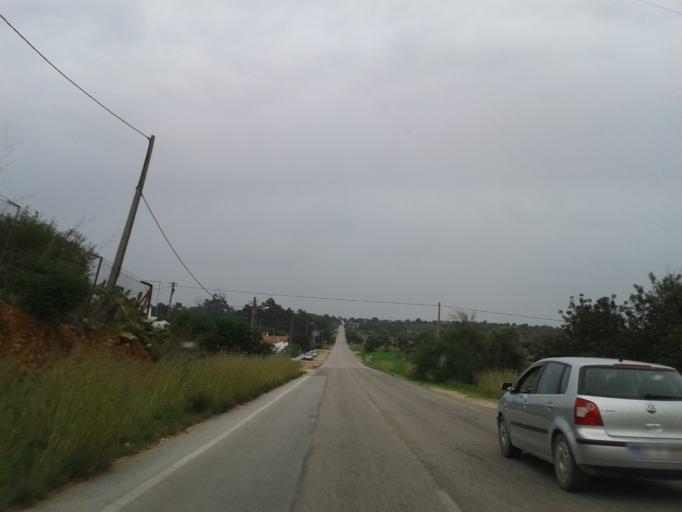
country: PT
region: Faro
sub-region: Silves
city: Silves
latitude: 37.1754
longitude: -8.4202
